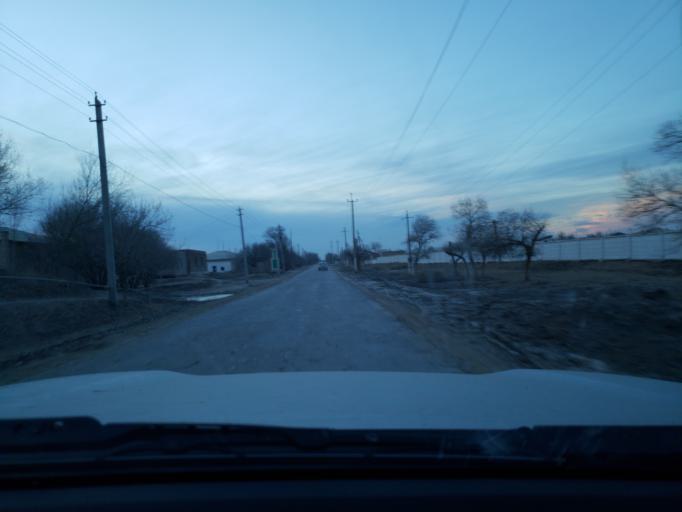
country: TM
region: Dasoguz
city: Tagta
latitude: 41.5839
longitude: 60.0641
